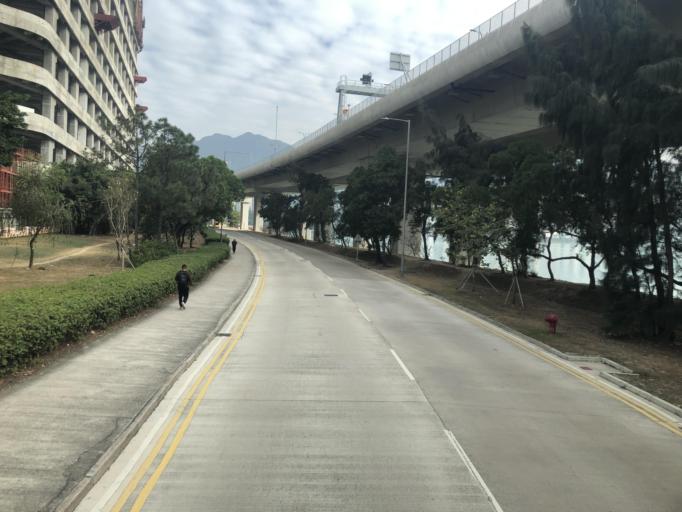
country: HK
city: Tai O
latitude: 22.2929
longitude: 113.9260
